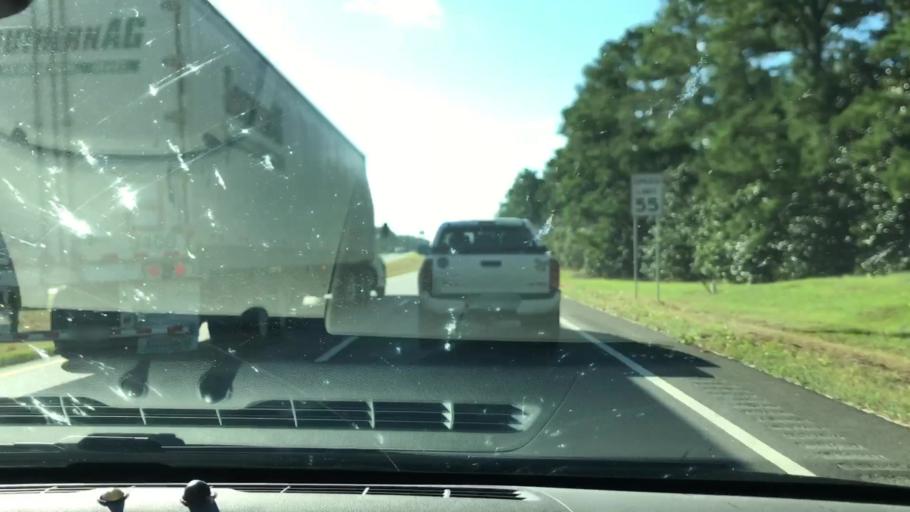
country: US
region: Georgia
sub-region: Lee County
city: Leesburg
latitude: 31.6495
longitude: -84.2626
